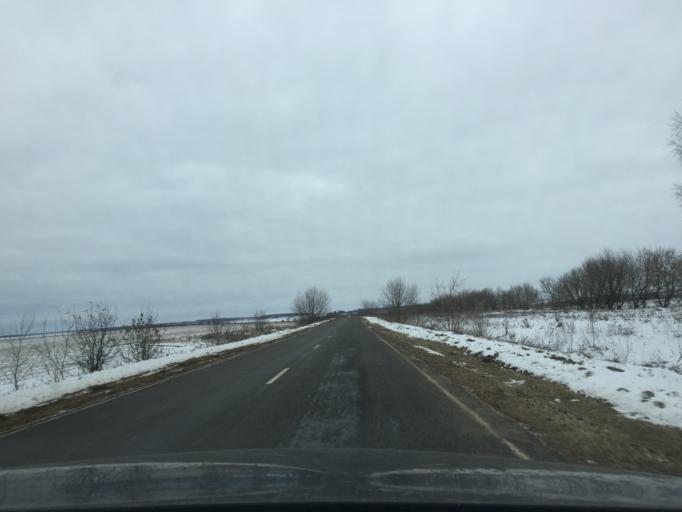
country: RU
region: Tula
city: Teploye
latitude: 53.7999
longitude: 37.5897
